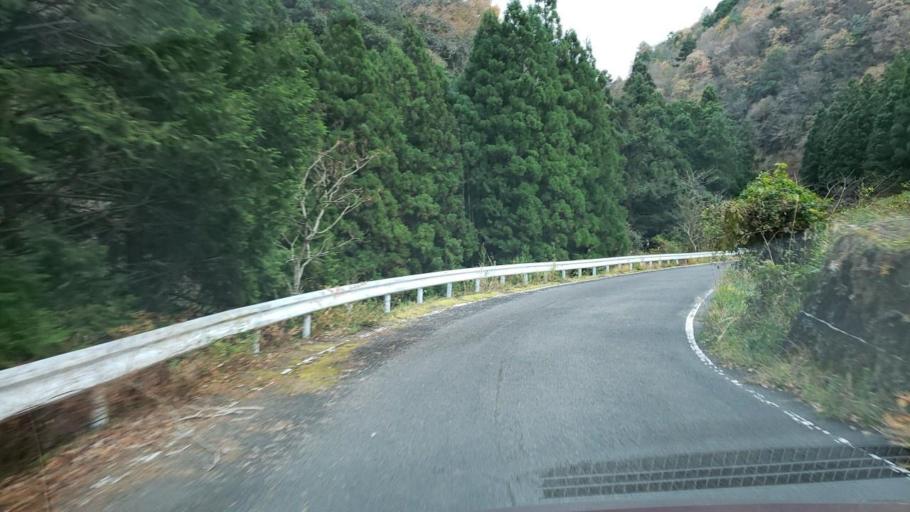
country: JP
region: Tokushima
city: Wakimachi
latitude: 34.1448
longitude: 134.2291
